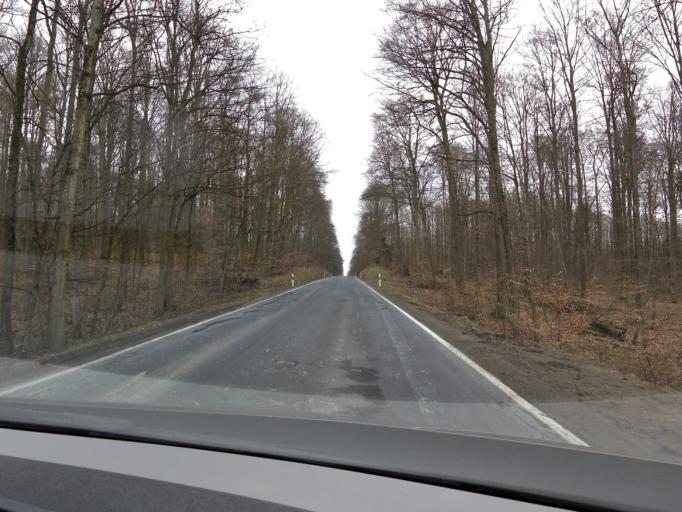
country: DE
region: Bavaria
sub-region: Regierungsbezirk Unterfranken
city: Rimpar
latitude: 49.9117
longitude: 9.9679
